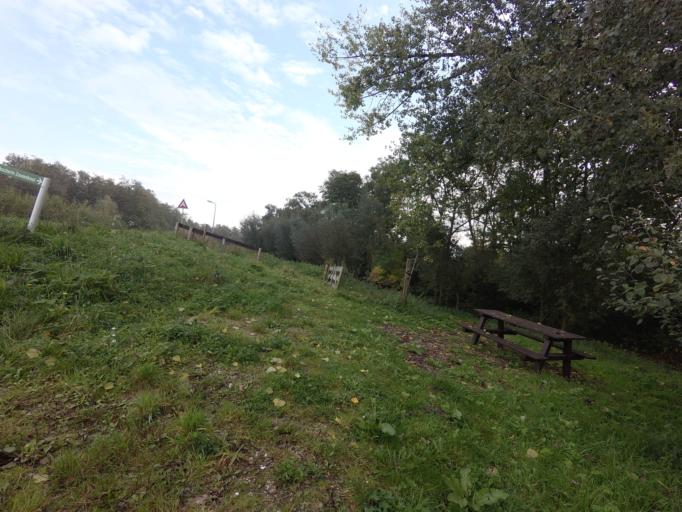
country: NL
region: Utrecht
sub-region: Gemeente Lopik
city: Lopik
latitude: 51.9546
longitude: 4.9796
